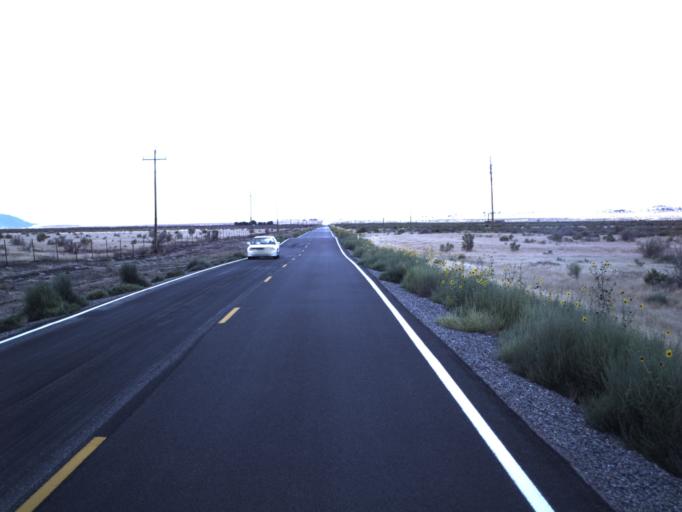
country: US
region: Utah
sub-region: Tooele County
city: Grantsville
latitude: 40.2592
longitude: -112.6938
